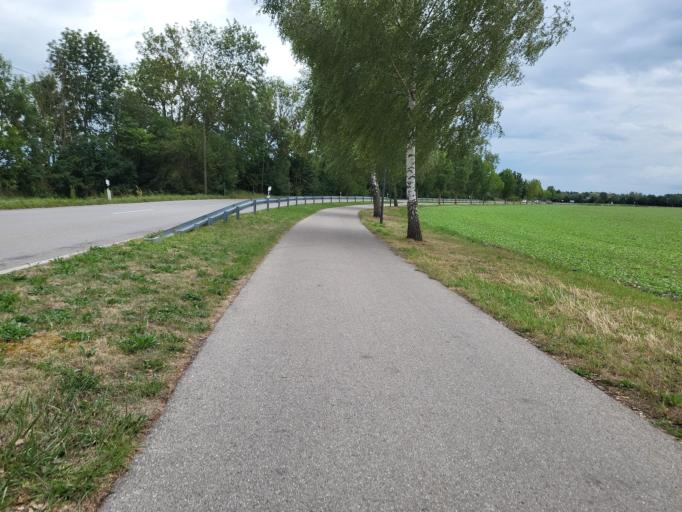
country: DE
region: Bavaria
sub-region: Upper Bavaria
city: Grobenzell
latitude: 48.2191
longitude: 11.3566
